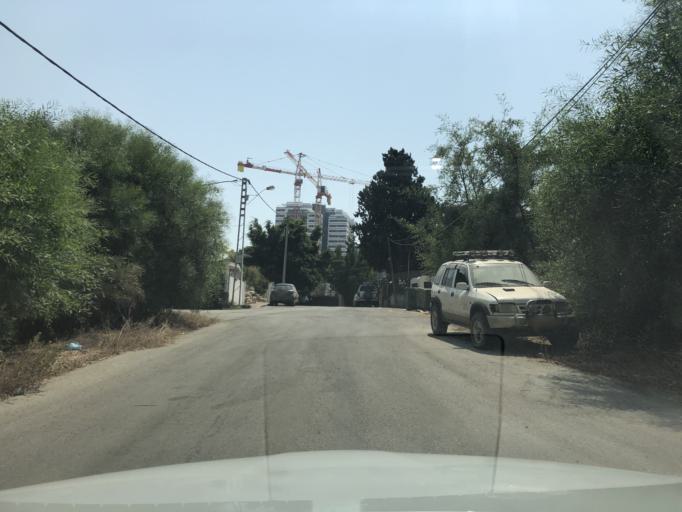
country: IL
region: Central District
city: Ganne Tiqwa
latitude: 32.0687
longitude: 34.8747
